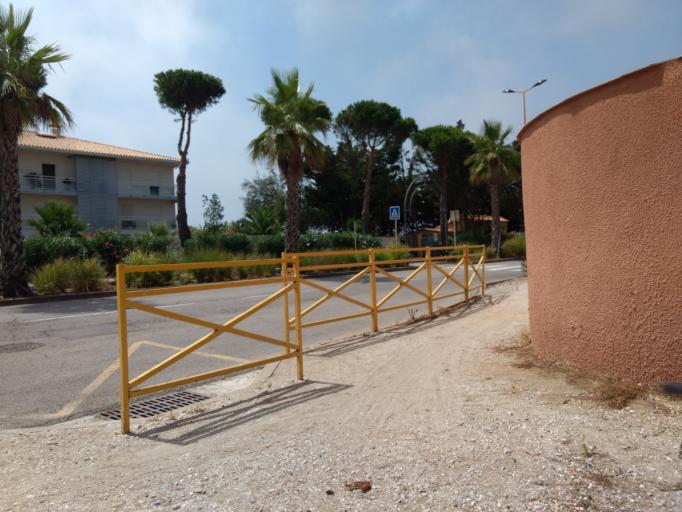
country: FR
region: Languedoc-Roussillon
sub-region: Departement des Pyrenees-Orientales
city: Le Barcares
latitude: 42.7919
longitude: 3.0301
